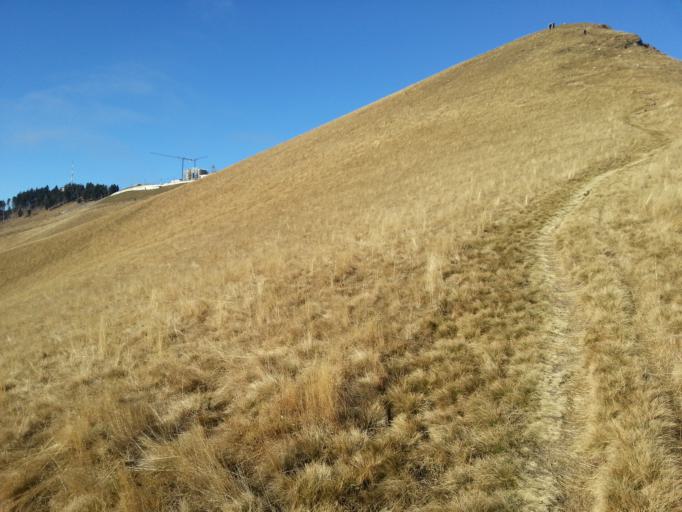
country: CH
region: Ticino
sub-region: Lugano District
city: Melano
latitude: 45.9276
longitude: 9.0281
